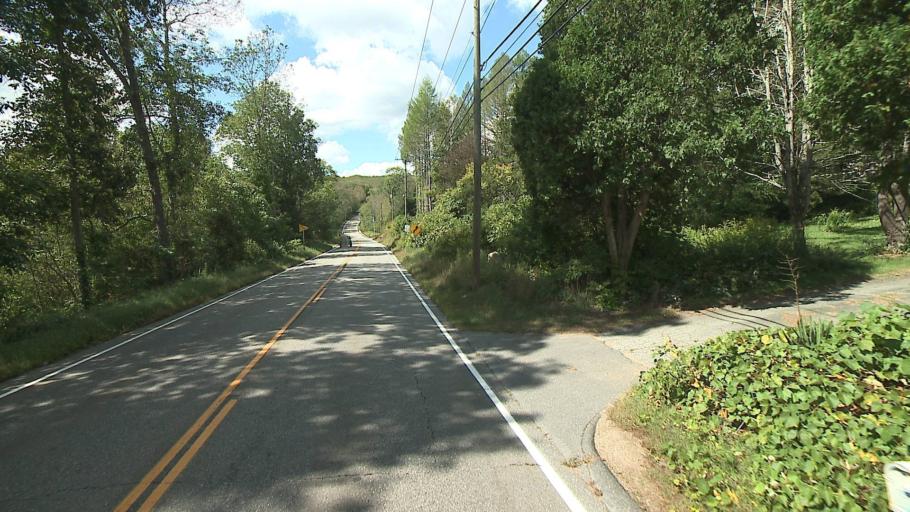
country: US
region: Connecticut
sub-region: Windham County
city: South Woodstock
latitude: 41.8793
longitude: -72.0969
